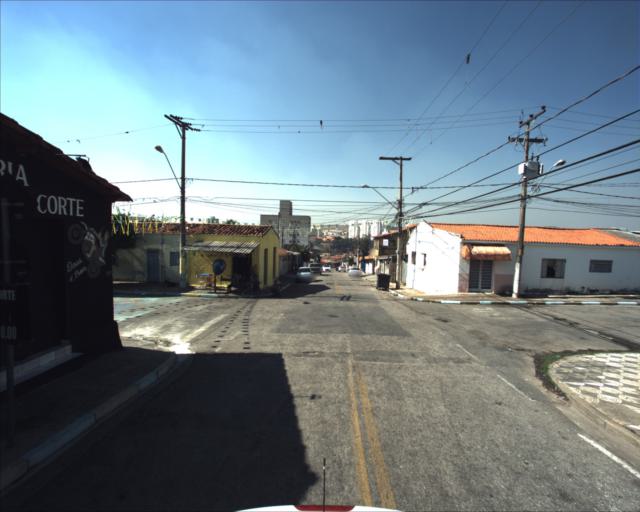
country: BR
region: Sao Paulo
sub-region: Sorocaba
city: Sorocaba
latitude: -23.4995
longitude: -47.4363
